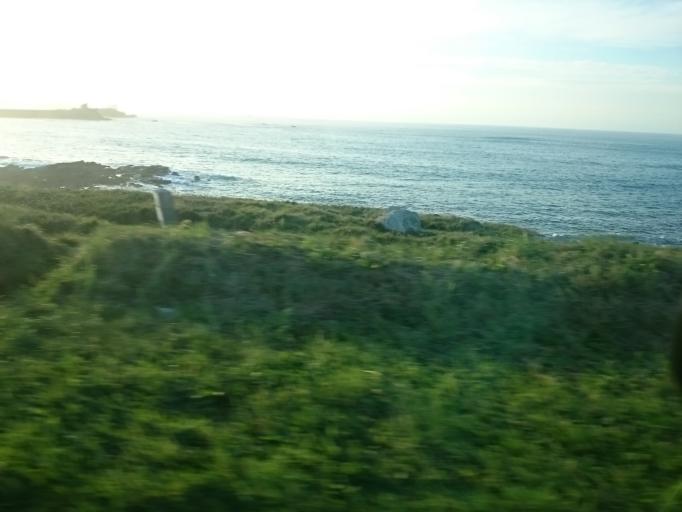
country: FR
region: Brittany
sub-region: Departement du Finistere
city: Landunvez
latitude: 48.5367
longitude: -4.7483
